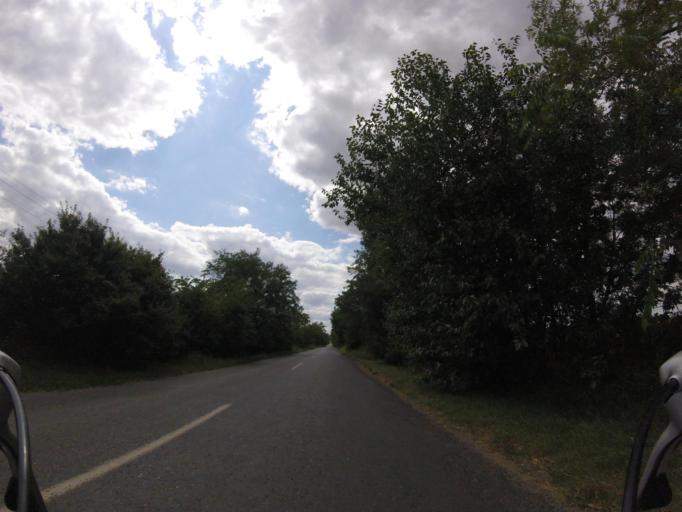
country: HU
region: Bacs-Kiskun
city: Tompa
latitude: 46.1769
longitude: 19.5203
